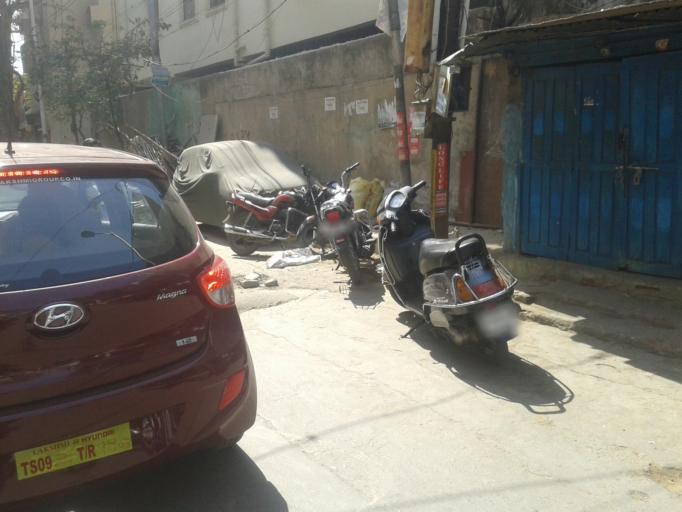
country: IN
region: Telangana
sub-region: Hyderabad
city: Hyderabad
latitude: 17.4068
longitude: 78.4822
